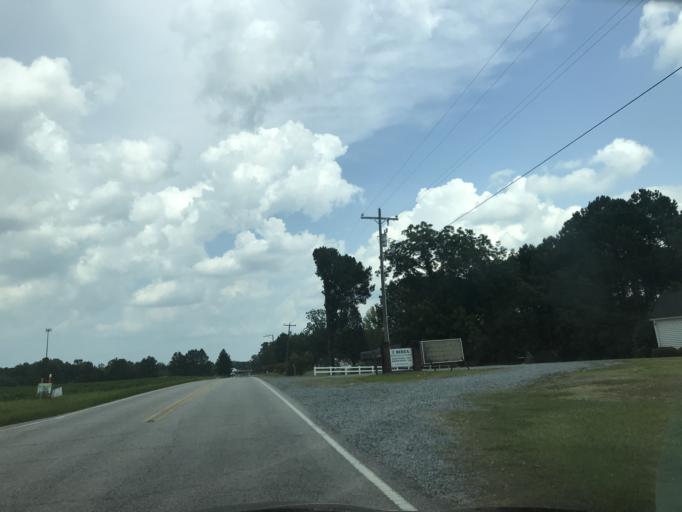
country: US
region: North Carolina
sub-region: Johnston County
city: Four Oaks
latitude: 35.5112
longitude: -78.5271
